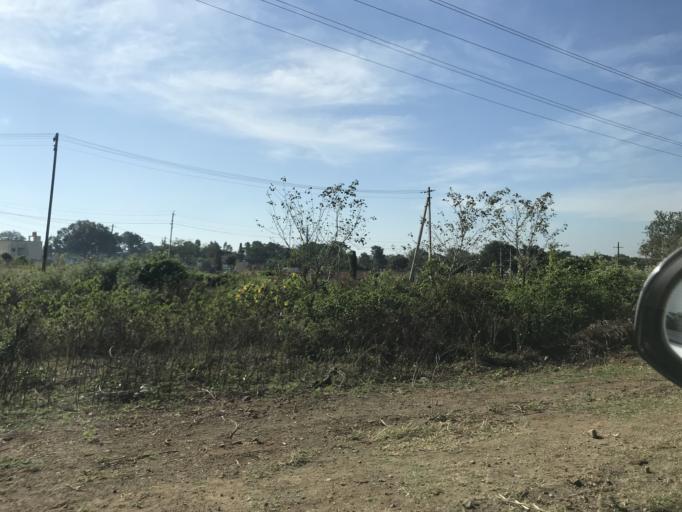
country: IN
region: Karnataka
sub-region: Mysore
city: Mysore
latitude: 12.2176
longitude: 76.5699
